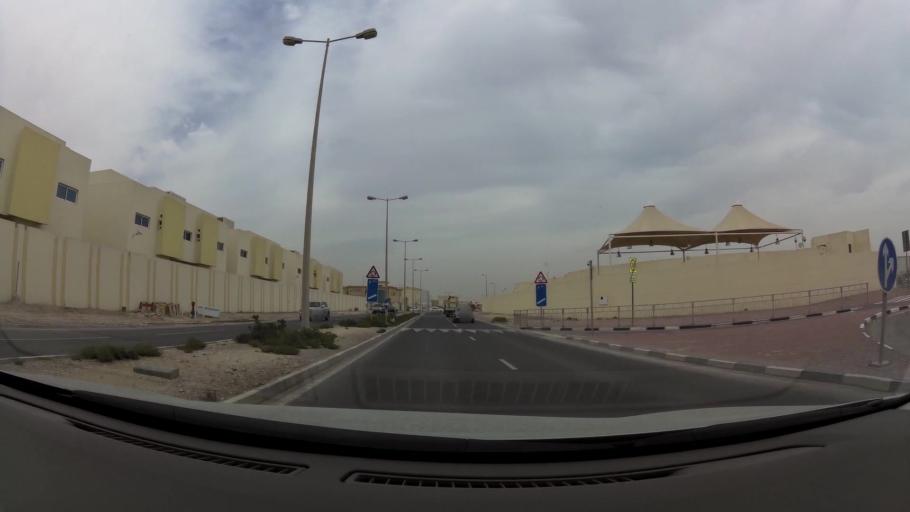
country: QA
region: Baladiyat ad Dawhah
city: Doha
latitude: 25.2347
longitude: 51.4685
